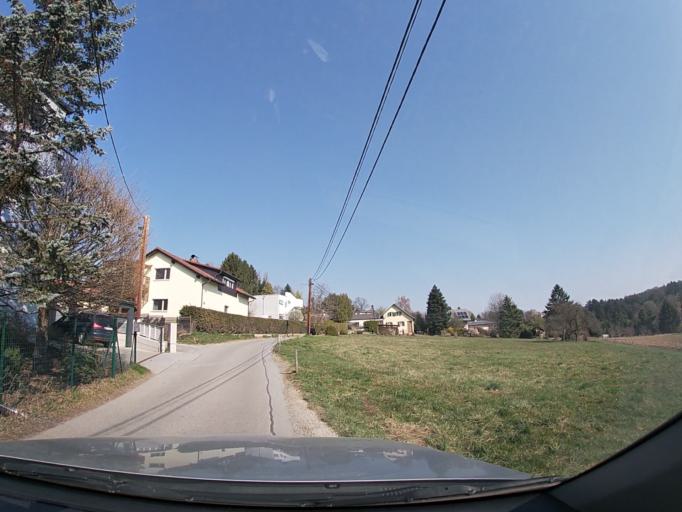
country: AT
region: Styria
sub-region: Politischer Bezirk Graz-Umgebung
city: Raaba
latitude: 47.0444
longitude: 15.4919
